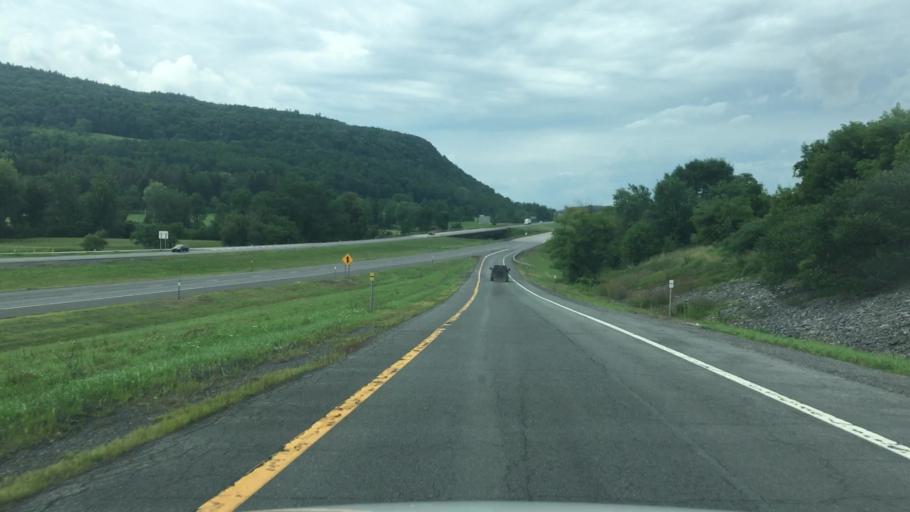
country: US
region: New York
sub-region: Schoharie County
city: Schoharie
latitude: 42.7070
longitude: -74.3175
